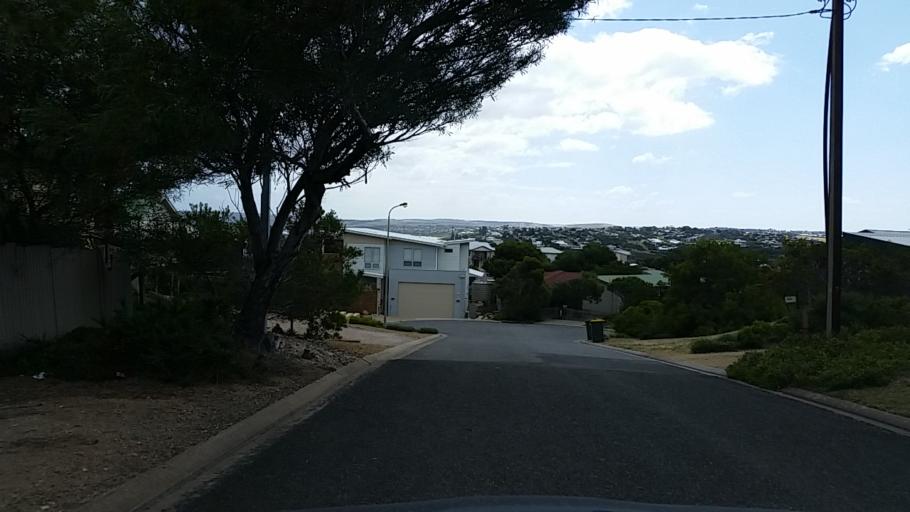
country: AU
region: South Australia
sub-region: Alexandrina
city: Port Elliot
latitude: -35.5338
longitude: 138.6725
